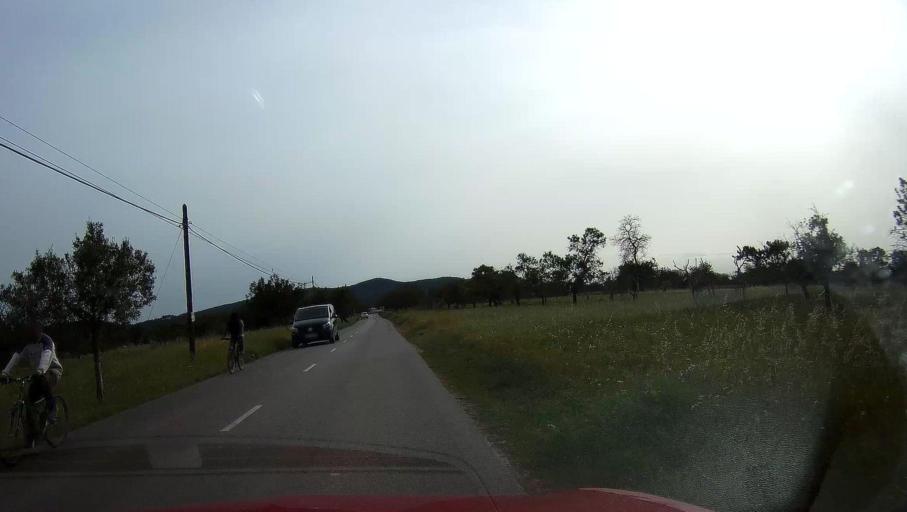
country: ES
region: Balearic Islands
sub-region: Illes Balears
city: Sant Joan de Labritja
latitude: 39.0361
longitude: 1.5398
